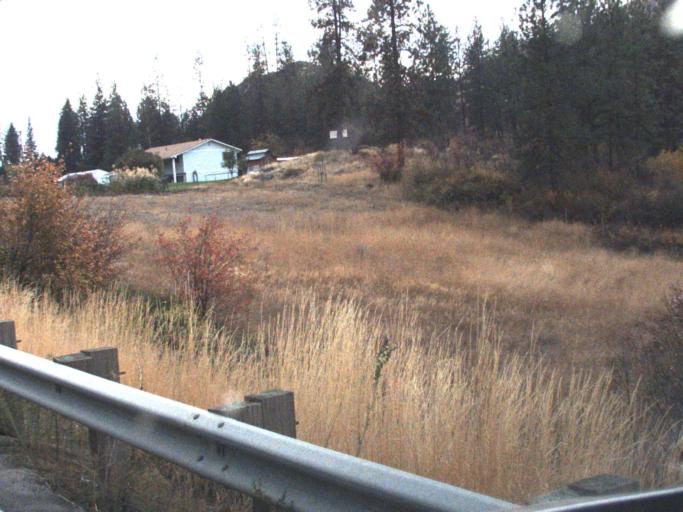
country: US
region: Washington
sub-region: Lincoln County
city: Davenport
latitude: 48.1139
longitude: -118.2015
